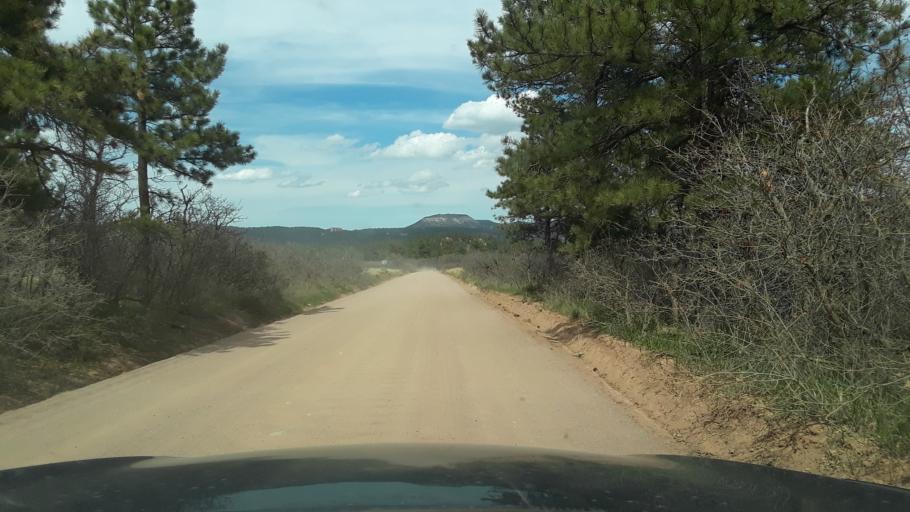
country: US
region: Colorado
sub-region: El Paso County
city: Palmer Lake
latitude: 39.0889
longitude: -104.9106
